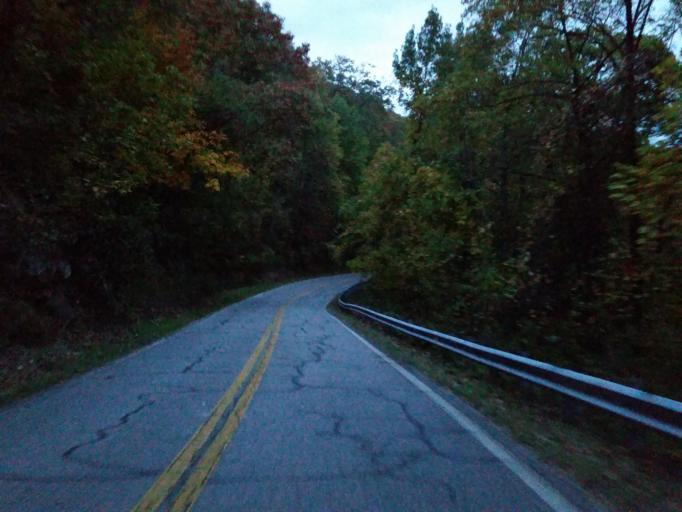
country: US
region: Georgia
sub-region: Lumpkin County
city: Dahlonega
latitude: 34.6434
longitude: -83.9620
